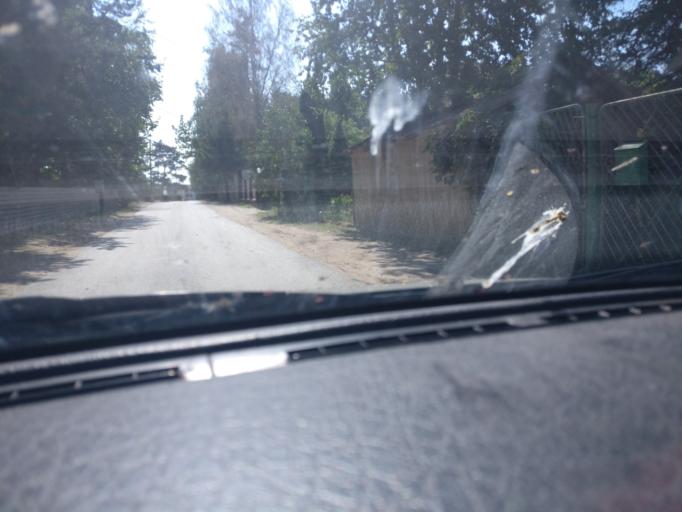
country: EE
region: Tartu
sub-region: Tartu linn
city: Tartu
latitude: 58.3497
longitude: 26.7895
